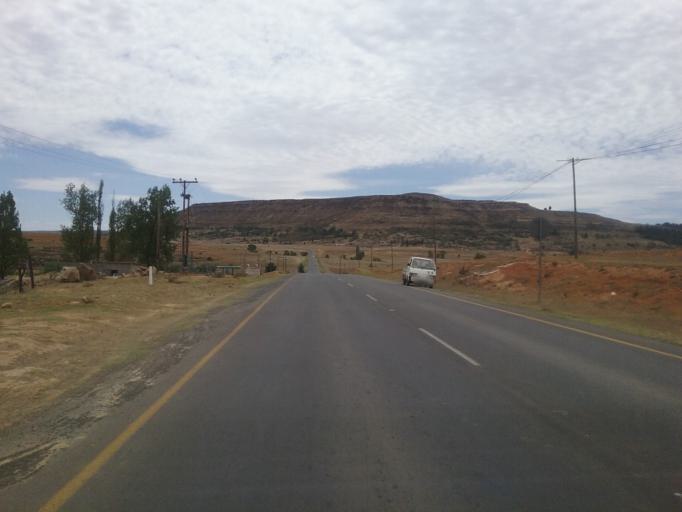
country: LS
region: Maseru
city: Nako
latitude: -29.6192
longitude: 27.4977
